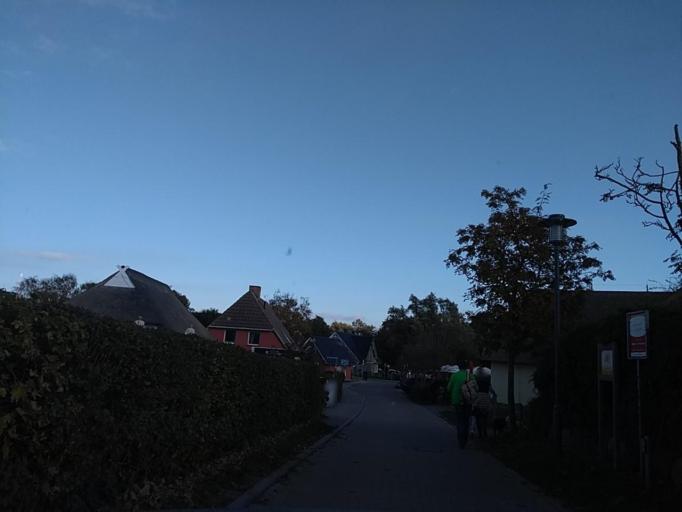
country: DE
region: Mecklenburg-Vorpommern
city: Ostseebad Dierhagen
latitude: 54.3789
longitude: 12.4163
